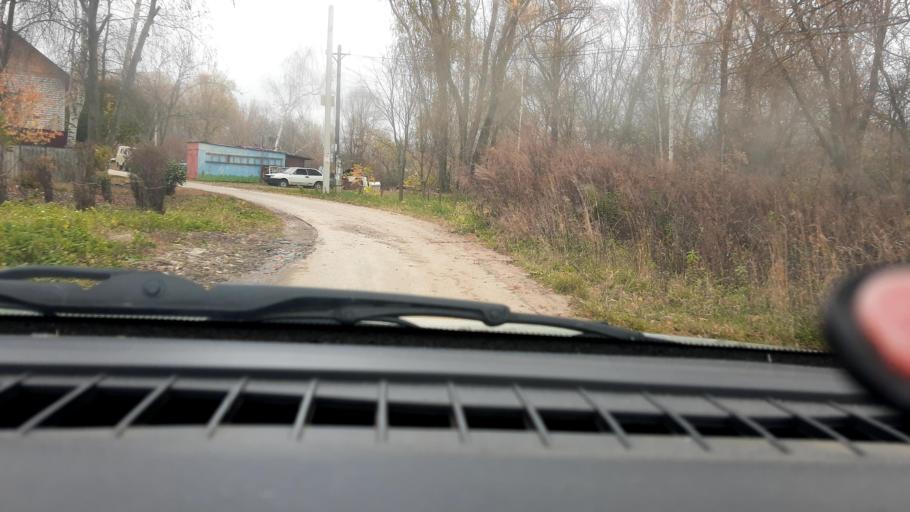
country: RU
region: Nizjnij Novgorod
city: Afonino
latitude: 56.2712
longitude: 44.1048
